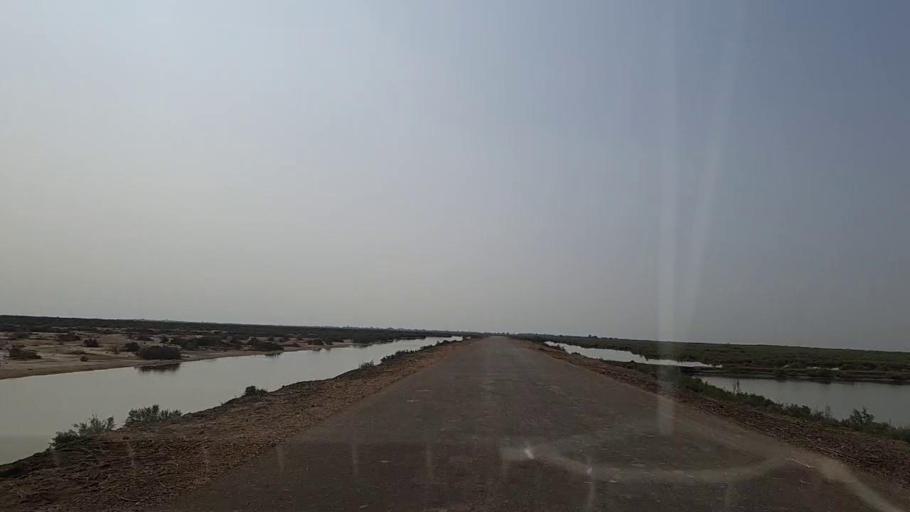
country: PK
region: Sindh
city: Chuhar Jamali
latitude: 24.2185
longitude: 67.8711
